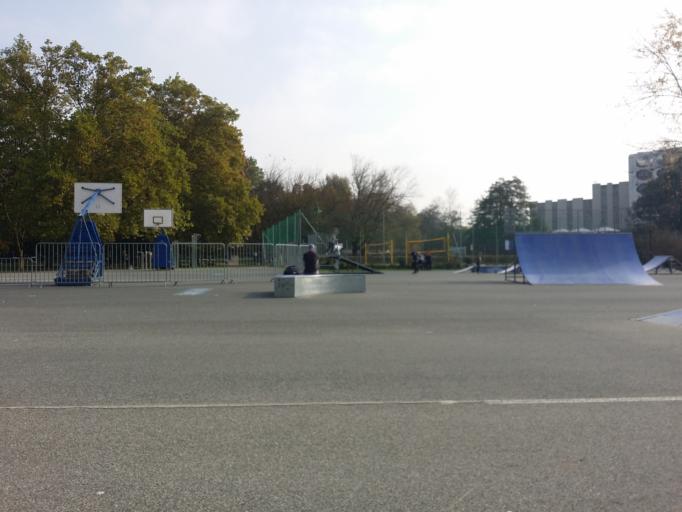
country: AT
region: Carinthia
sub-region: Klagenfurt am Woerthersee
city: Klagenfurt am Woerthersee
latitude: 46.6186
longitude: 14.2588
